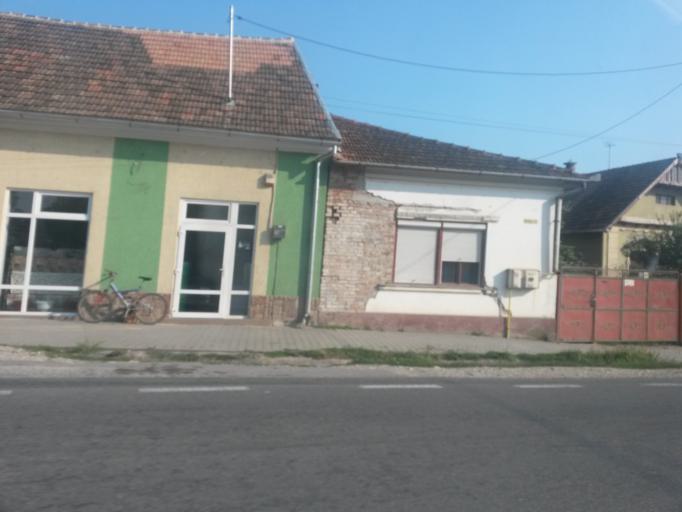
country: RO
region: Alba
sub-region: Comuna Unirea
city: Unirea
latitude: 46.4032
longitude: 23.8111
